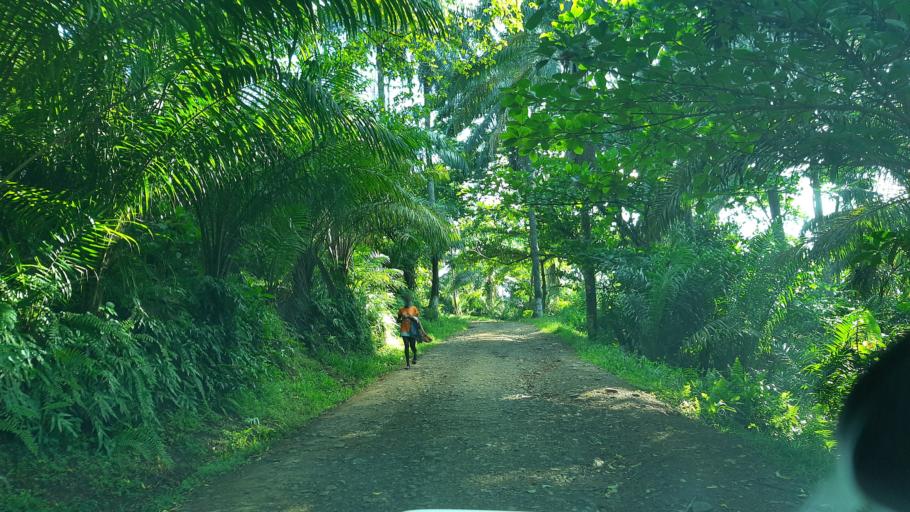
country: ST
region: Sao Tome Island
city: Sao Tome
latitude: 0.2451
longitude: 6.7382
